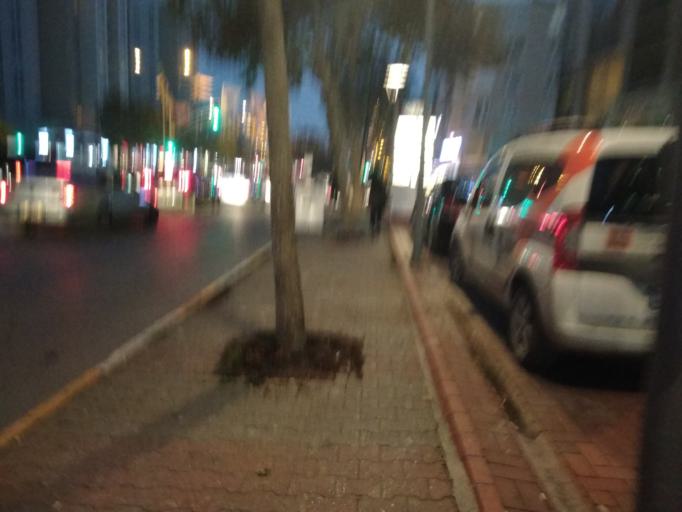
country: TR
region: Istanbul
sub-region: Atasehir
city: Atasehir
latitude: 40.9784
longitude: 29.1203
